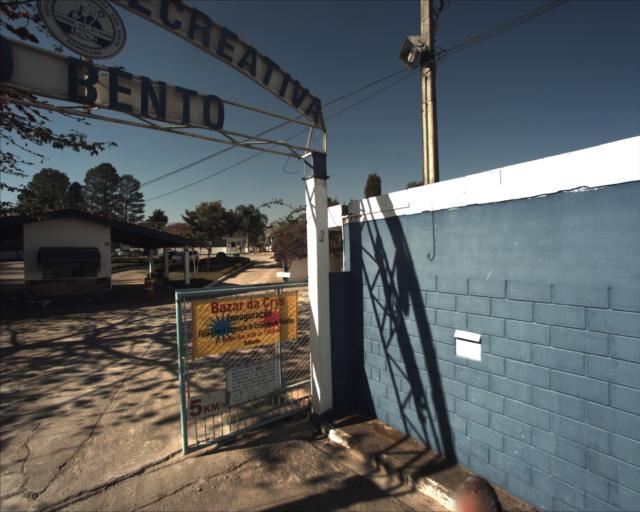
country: BR
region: Sao Paulo
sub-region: Sorocaba
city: Sorocaba
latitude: -23.5126
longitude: -47.4281
